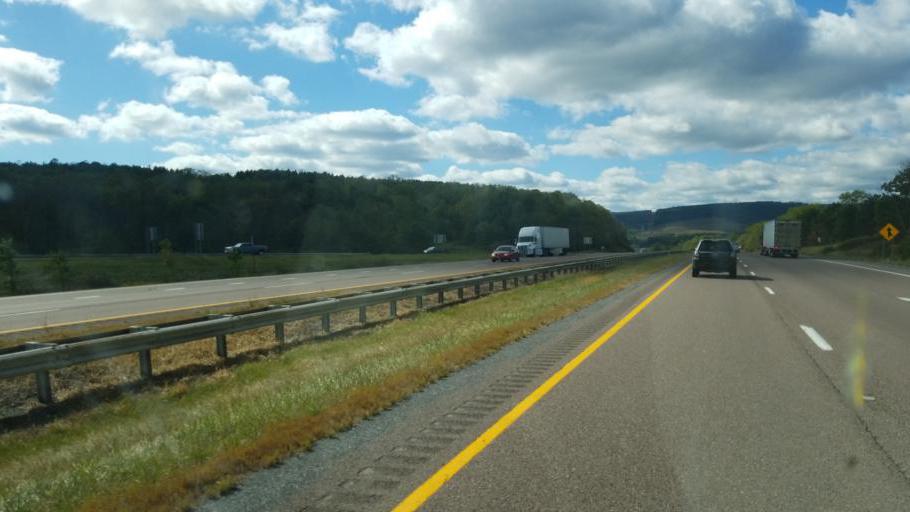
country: US
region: Maryland
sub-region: Allegany County
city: Frostburg
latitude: 39.6330
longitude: -78.9189
